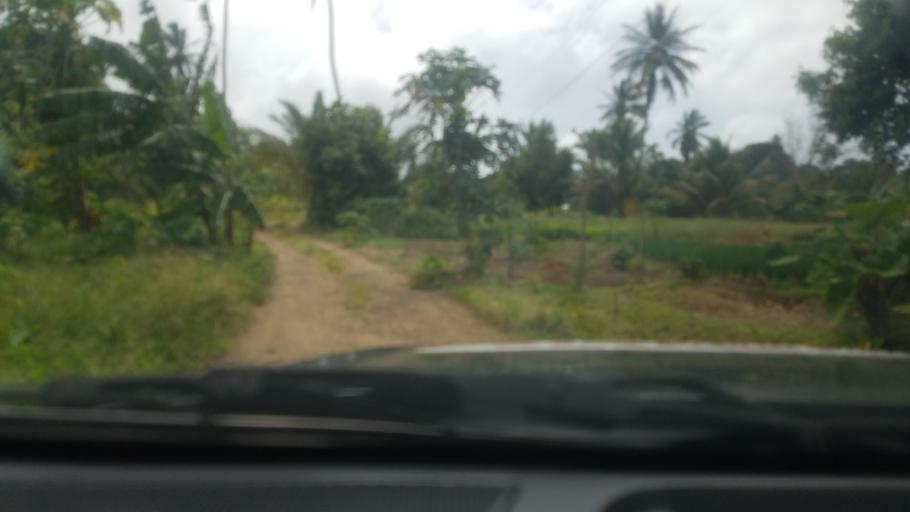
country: LC
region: Micoud Quarter
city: Micoud
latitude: 13.8039
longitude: -60.9504
